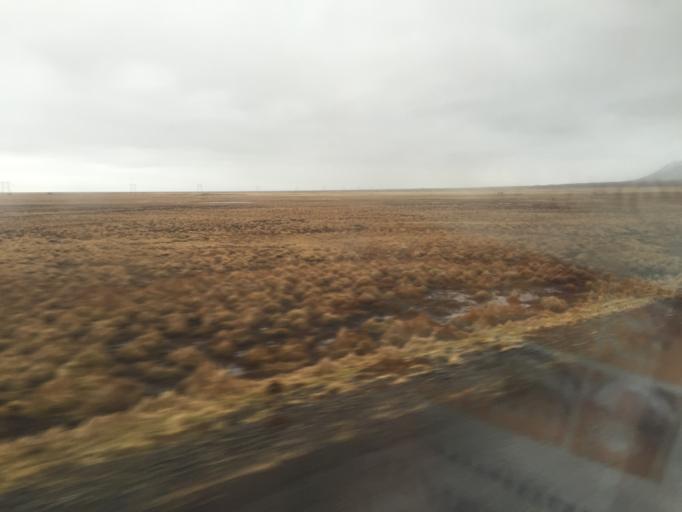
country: IS
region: East
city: Hoefn
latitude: 63.8903
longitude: -16.6985
